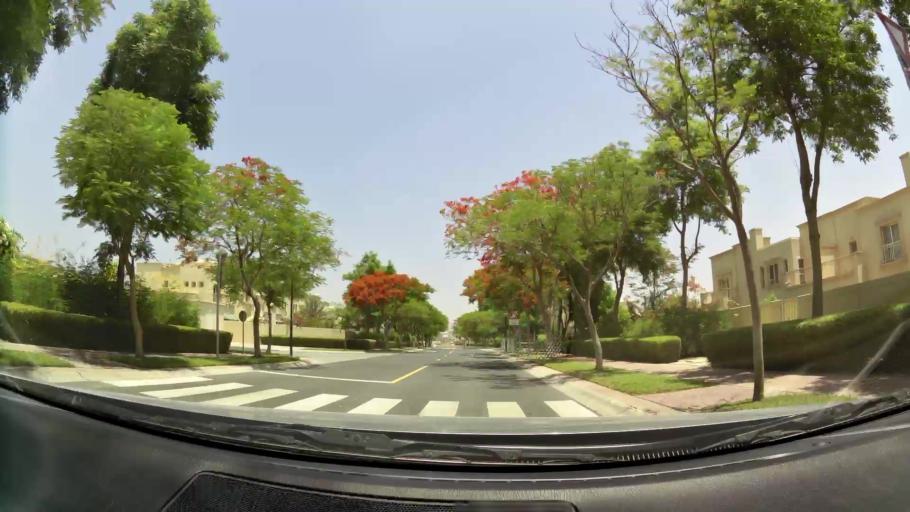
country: AE
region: Dubai
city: Dubai
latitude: 25.0594
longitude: 55.1867
